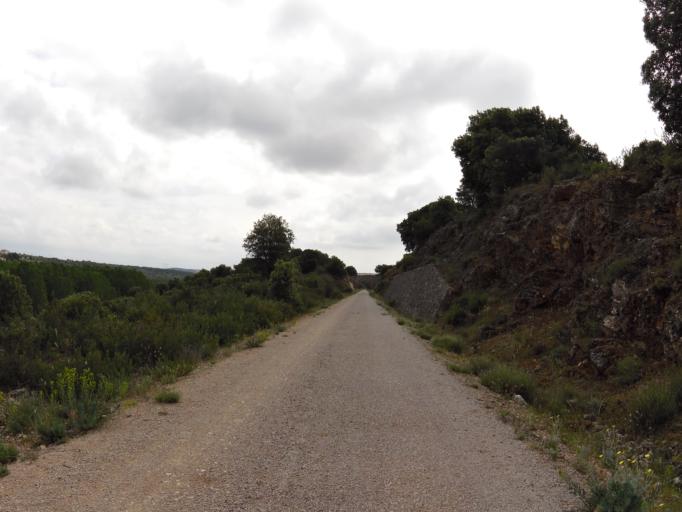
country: ES
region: Castille-La Mancha
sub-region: Provincia de Albacete
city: Robledo
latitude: 38.7710
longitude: -2.4219
